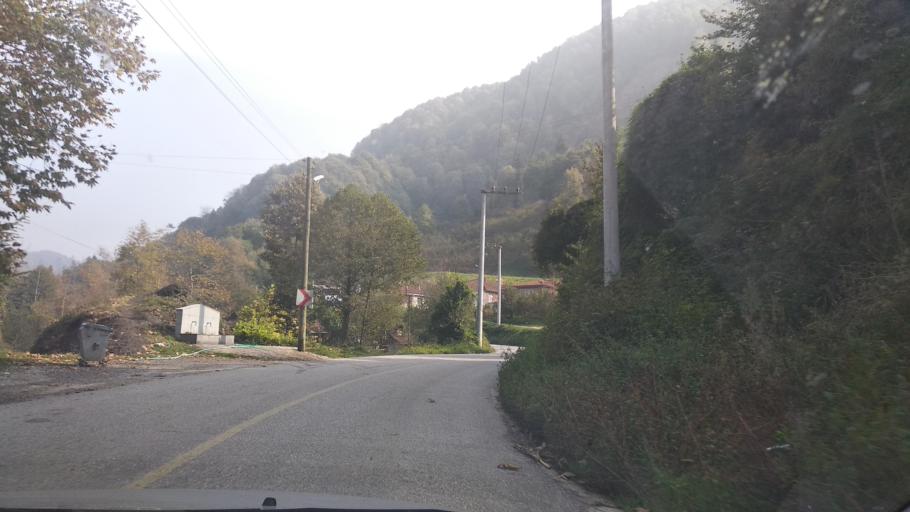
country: TR
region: Duzce
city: Kaynasli
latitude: 40.7347
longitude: 31.2140
